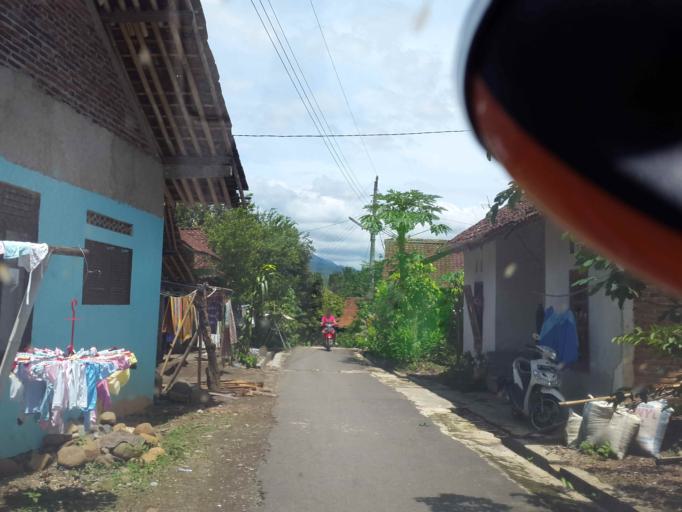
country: ID
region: Central Java
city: Wonosobo
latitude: -7.3777
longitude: 109.6452
